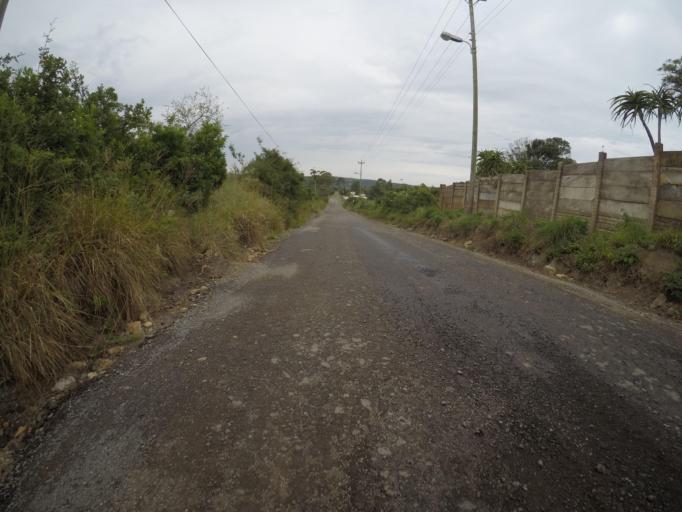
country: ZA
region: Eastern Cape
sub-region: Buffalo City Metropolitan Municipality
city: East London
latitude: -32.9607
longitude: 27.8415
